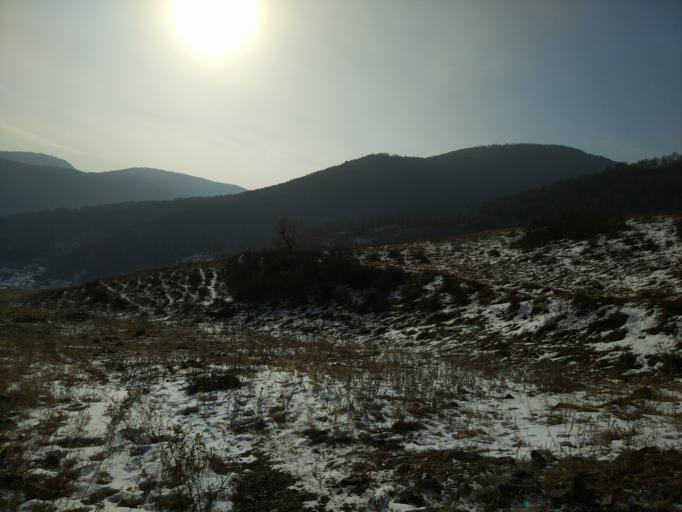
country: CN
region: Hebei
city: Xiwanzi
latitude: 40.8582
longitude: 115.4560
